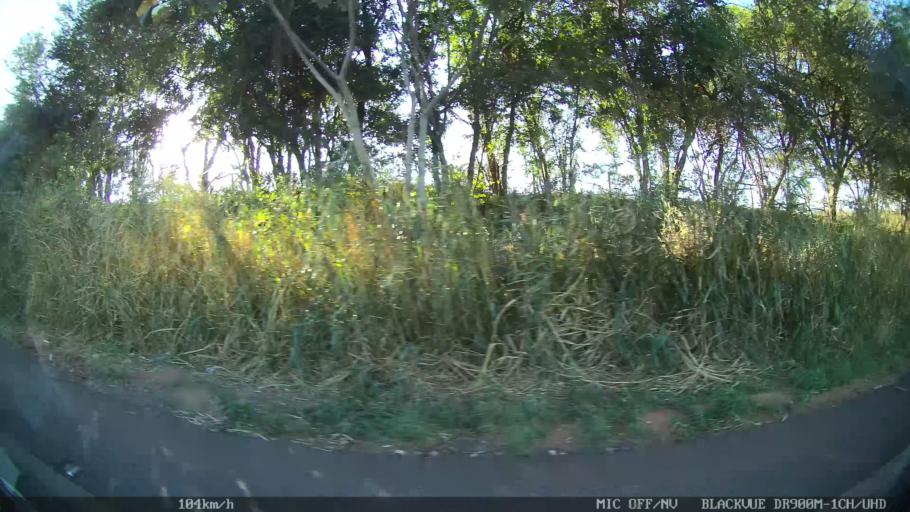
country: BR
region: Sao Paulo
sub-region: Guapiacu
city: Guapiacu
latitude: -20.7700
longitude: -49.2137
